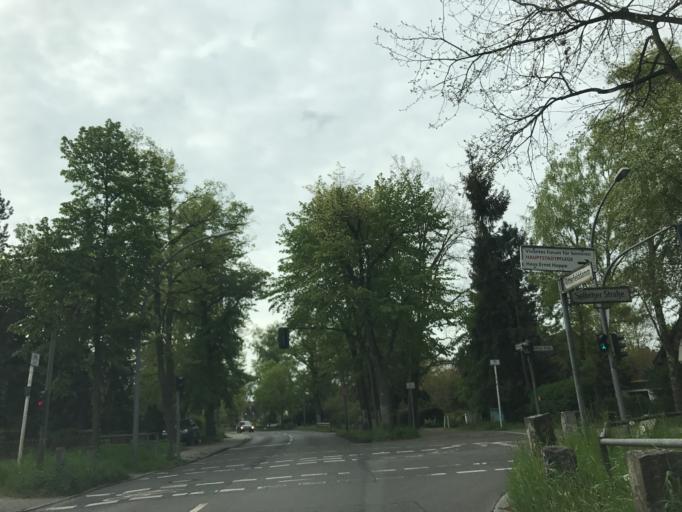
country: DE
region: Berlin
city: Kladow
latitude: 52.4645
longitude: 13.1299
